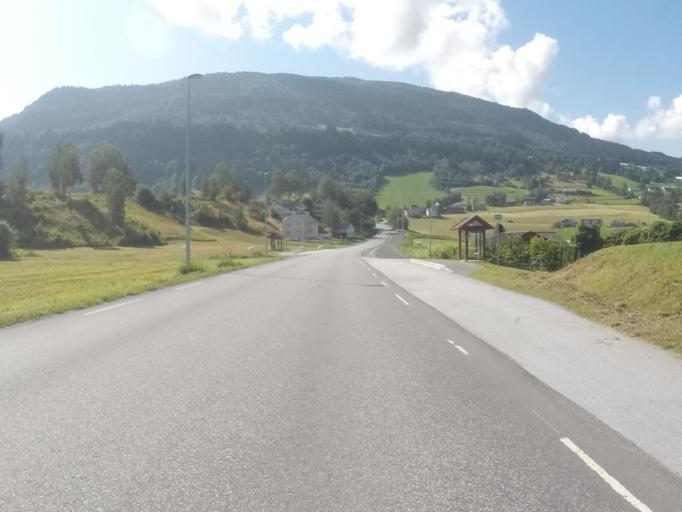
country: NO
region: Sogn og Fjordane
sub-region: Vik
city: Vikoyri
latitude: 61.0776
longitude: 6.5775
